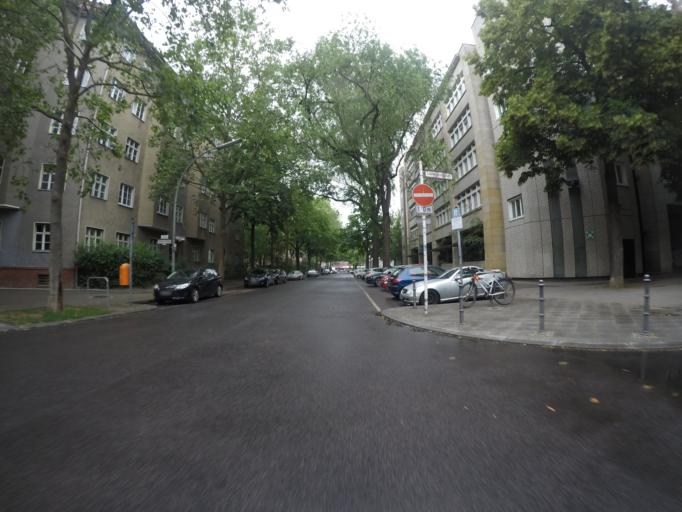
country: DE
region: Berlin
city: Wilmersdorf Bezirk
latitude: 52.4980
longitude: 13.3204
